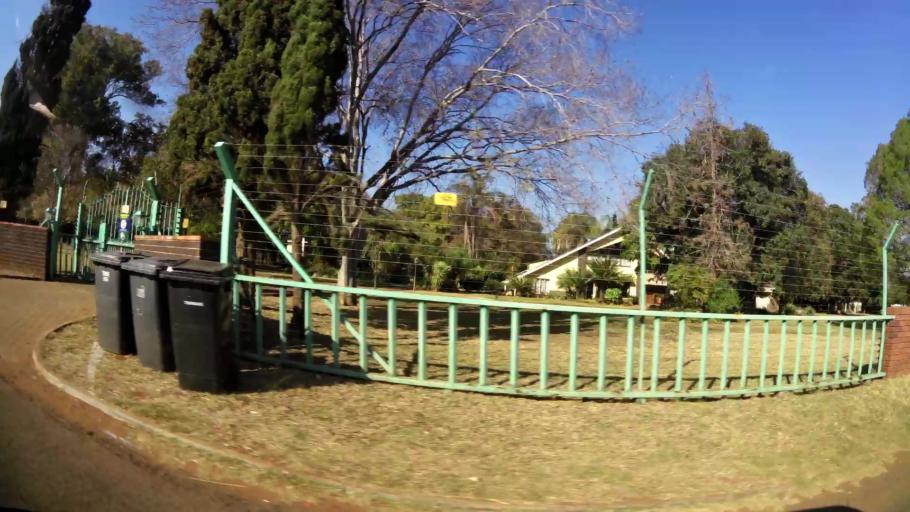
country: ZA
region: Gauteng
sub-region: City of Tshwane Metropolitan Municipality
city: Pretoria
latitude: -25.6480
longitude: 28.2202
